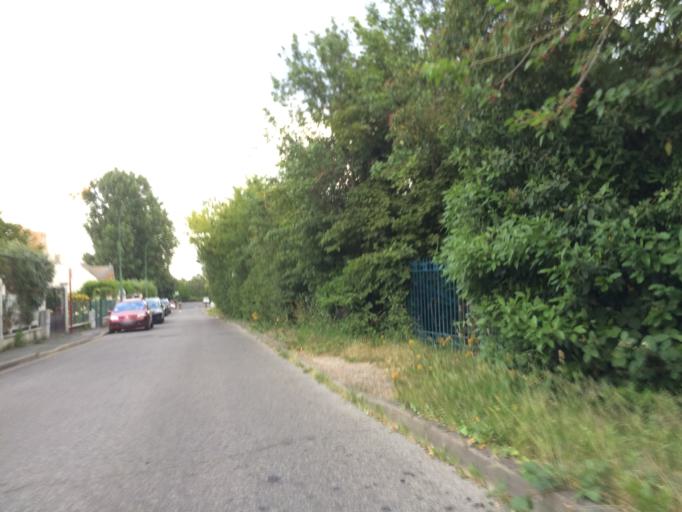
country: FR
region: Ile-de-France
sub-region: Departement de l'Essonne
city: Verrieres-le-Buisson
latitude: 48.7517
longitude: 2.2690
